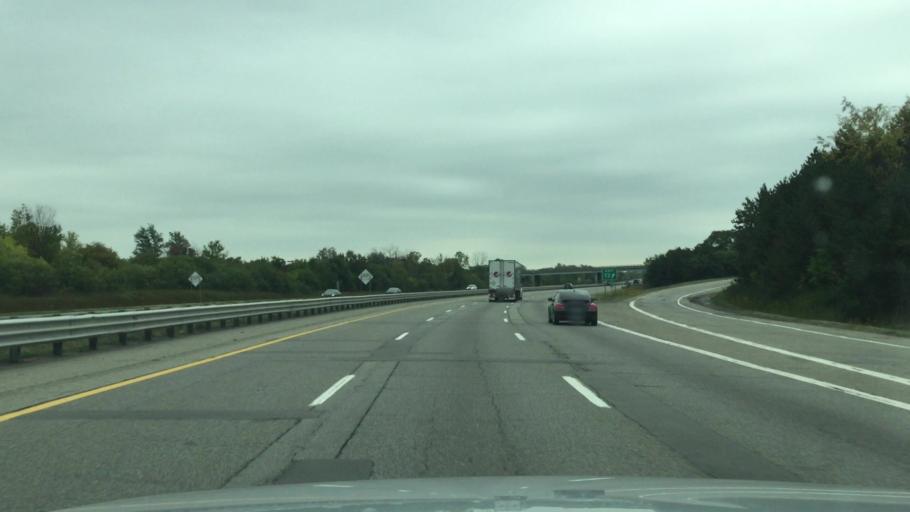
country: US
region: Michigan
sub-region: Oakland County
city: Troy
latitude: 42.6024
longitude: -83.1650
